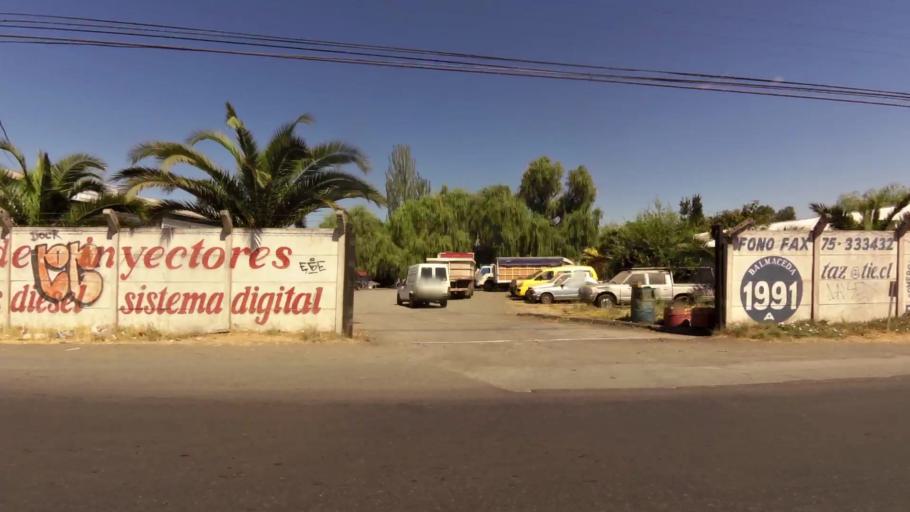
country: CL
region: Maule
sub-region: Provincia de Curico
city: Curico
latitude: -34.9670
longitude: -71.2485
